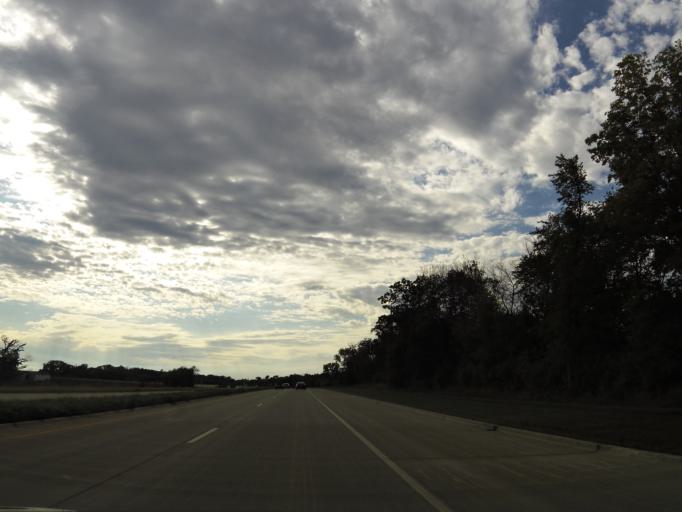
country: US
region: Minnesota
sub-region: Scott County
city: Prior Lake
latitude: 44.7724
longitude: -93.4266
